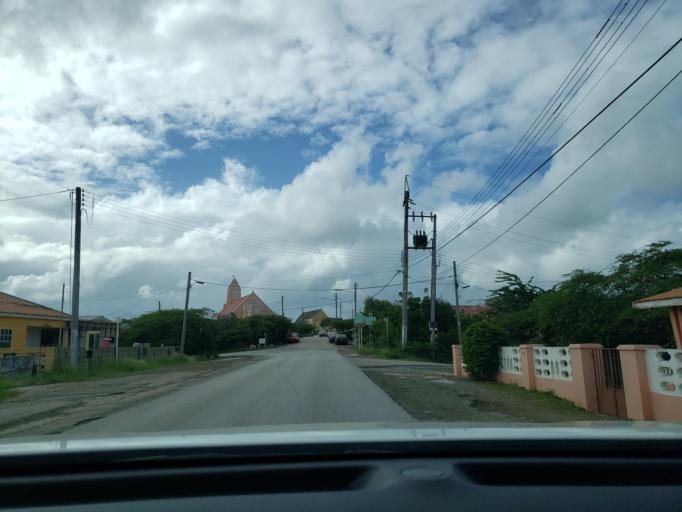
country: CW
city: Dorp Soto
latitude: 12.2160
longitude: -69.0629
